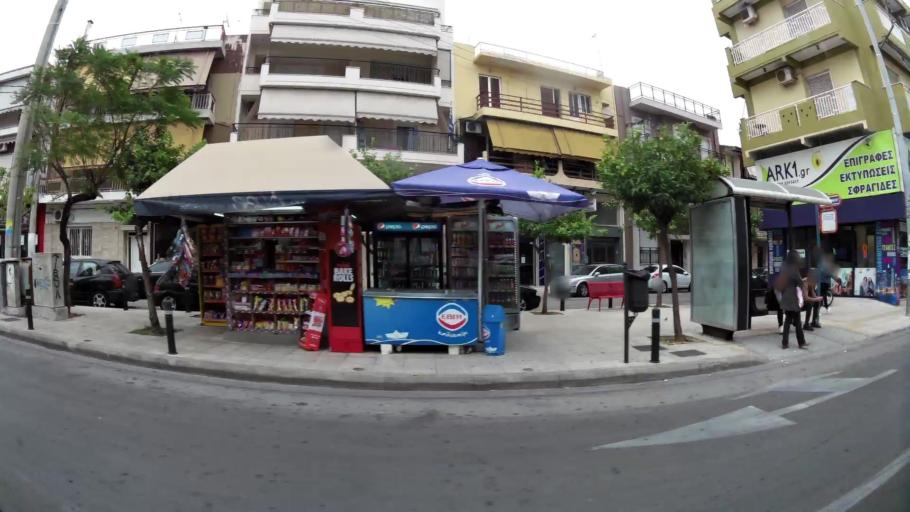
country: GR
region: Attica
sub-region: Nomarchia Athinas
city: Aigaleo
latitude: 37.9969
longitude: 23.6818
